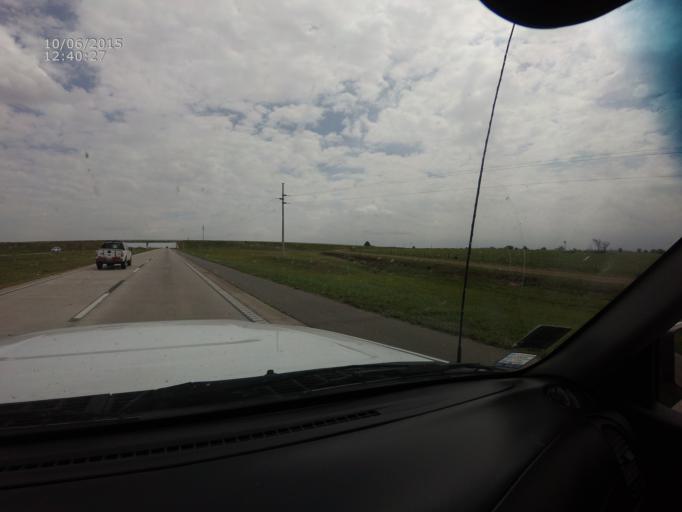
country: AR
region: Santa Fe
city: Canada de Gomez
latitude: -32.8646
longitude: -61.2846
